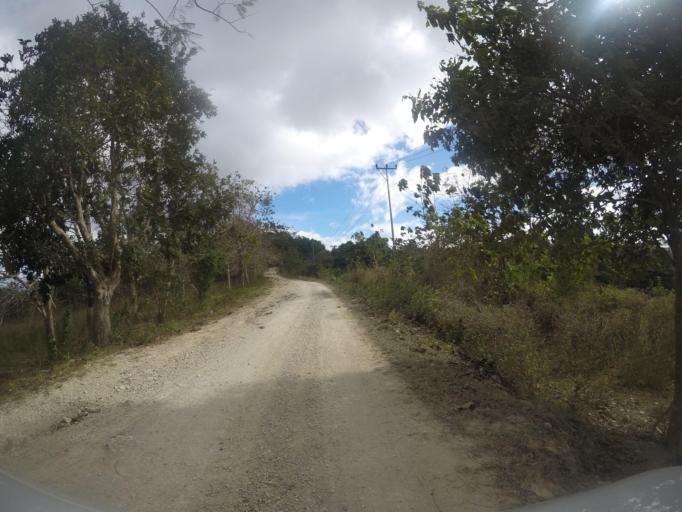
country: TL
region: Lautem
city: Lospalos
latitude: -8.5465
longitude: 126.9034
